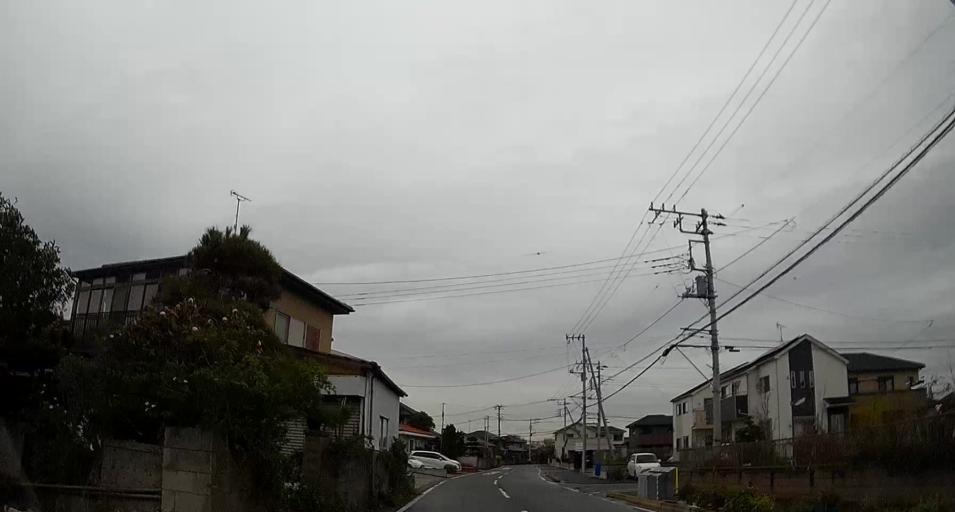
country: JP
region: Chiba
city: Kisarazu
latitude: 35.4379
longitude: 139.9257
